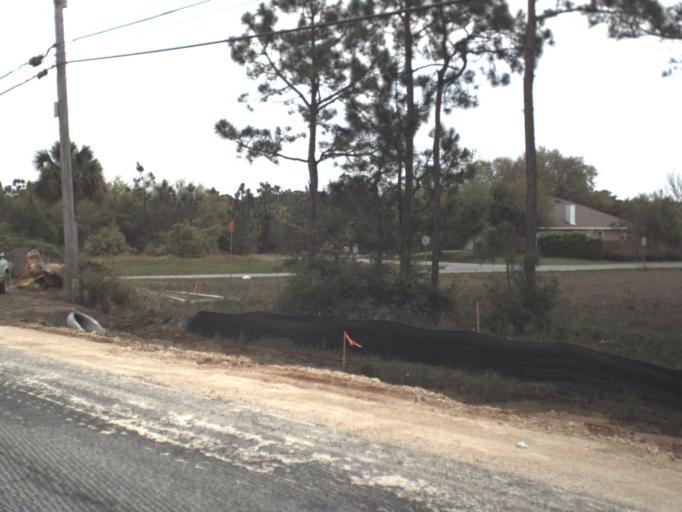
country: US
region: Florida
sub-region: Santa Rosa County
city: Woodlawn Beach
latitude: 30.4035
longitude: -86.9739
